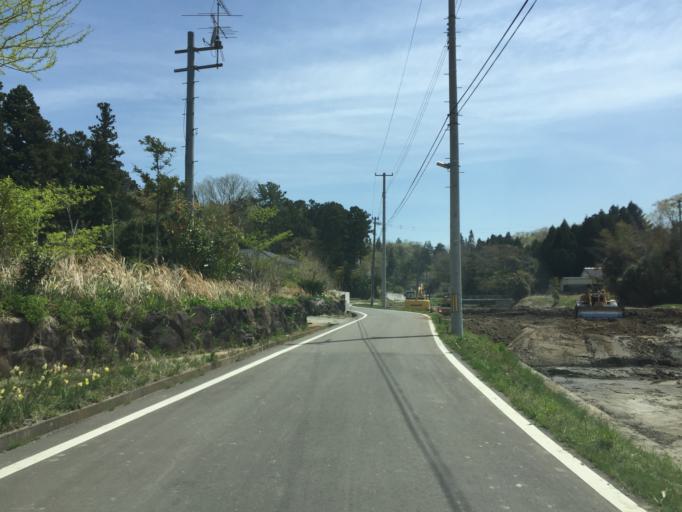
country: JP
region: Miyagi
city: Watari
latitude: 37.8991
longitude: 140.9258
